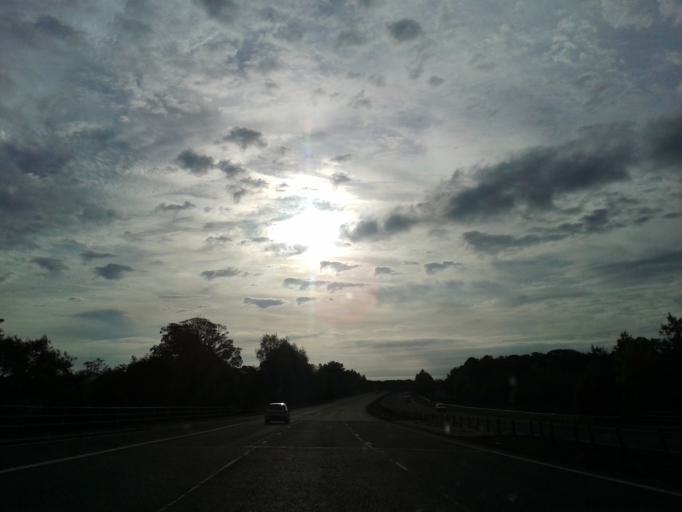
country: GB
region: Scotland
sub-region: Dumfries and Galloway
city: Annan
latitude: 55.0457
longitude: -3.1919
